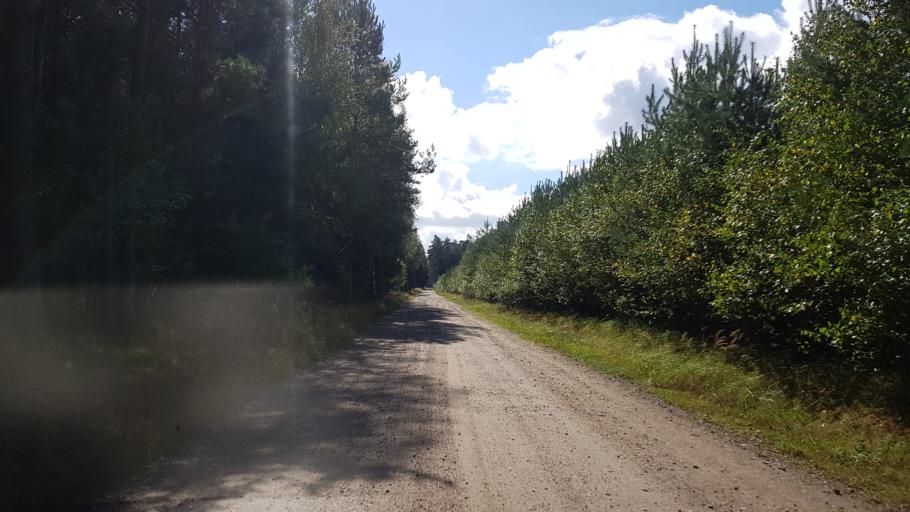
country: PL
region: West Pomeranian Voivodeship
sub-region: Powiat bialogardzki
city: Tychowo
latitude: 54.0313
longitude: 16.3020
